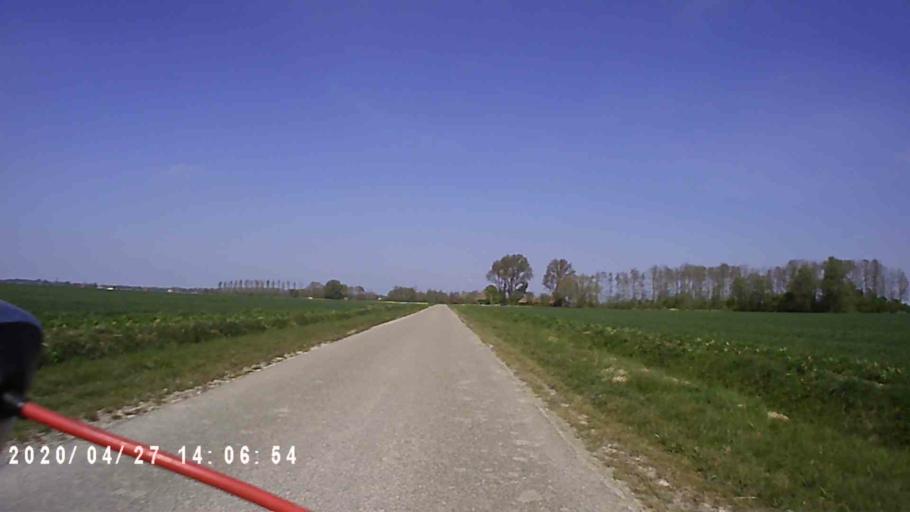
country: NL
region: Groningen
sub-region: Gemeente Zuidhorn
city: Oldehove
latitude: 53.3407
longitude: 6.3931
